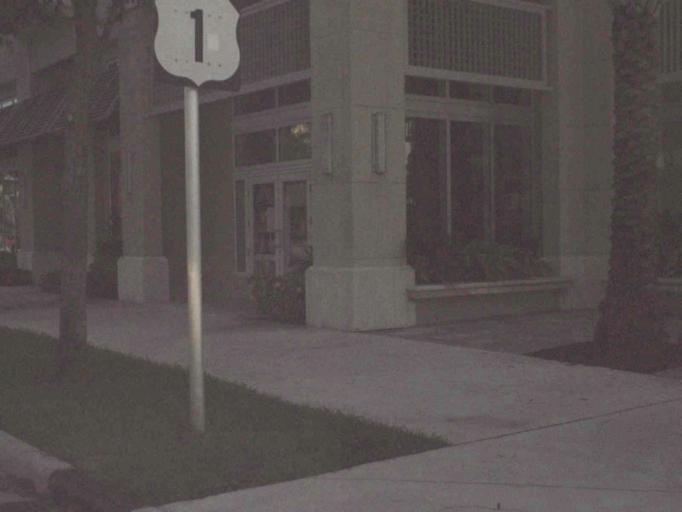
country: US
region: Florida
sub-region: Palm Beach County
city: West Palm Beach
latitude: 26.7076
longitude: -80.0550
